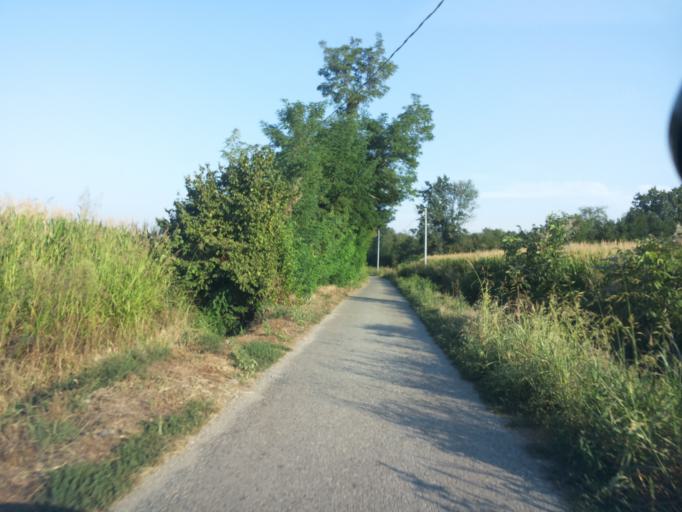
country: IT
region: Piedmont
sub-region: Provincia di Biella
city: Cavaglia
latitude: 45.3937
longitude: 8.1165
